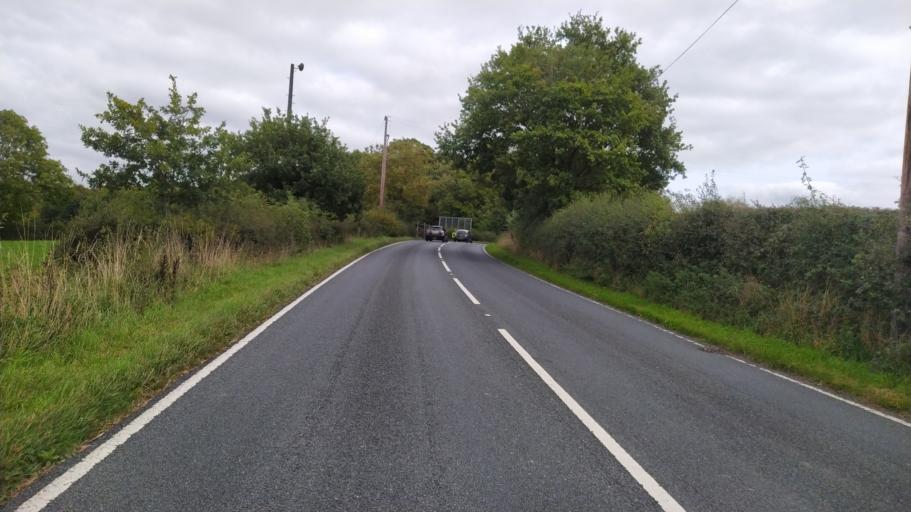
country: GB
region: England
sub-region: Dorset
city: Shaftesbury
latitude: 51.0167
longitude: -2.2270
